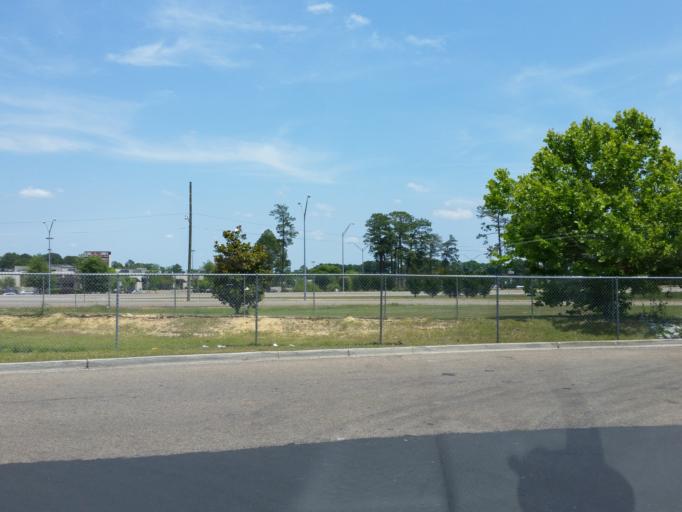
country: US
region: Mississippi
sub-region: Forrest County
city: Hattiesburg
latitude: 31.3088
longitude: -89.3195
